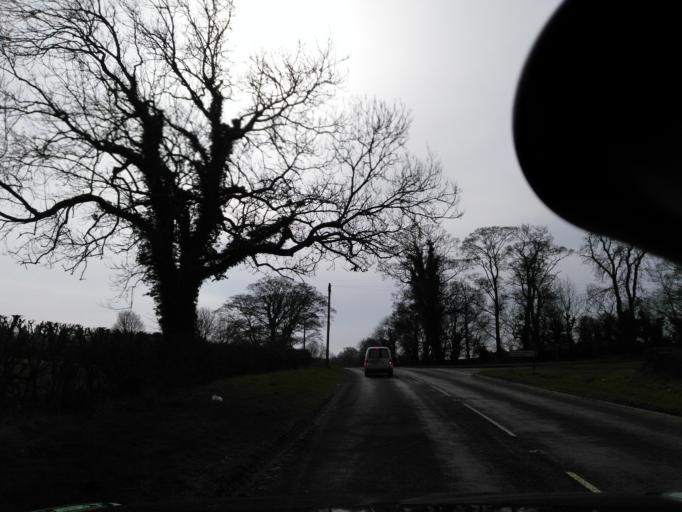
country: GB
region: England
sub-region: North Yorkshire
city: Northallerton
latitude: 54.2943
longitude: -1.3922
